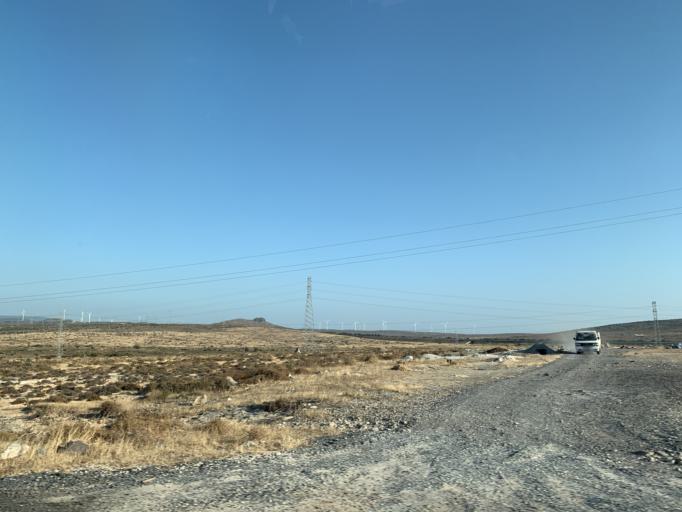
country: TR
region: Izmir
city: Alacati
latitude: 38.2778
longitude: 26.4275
